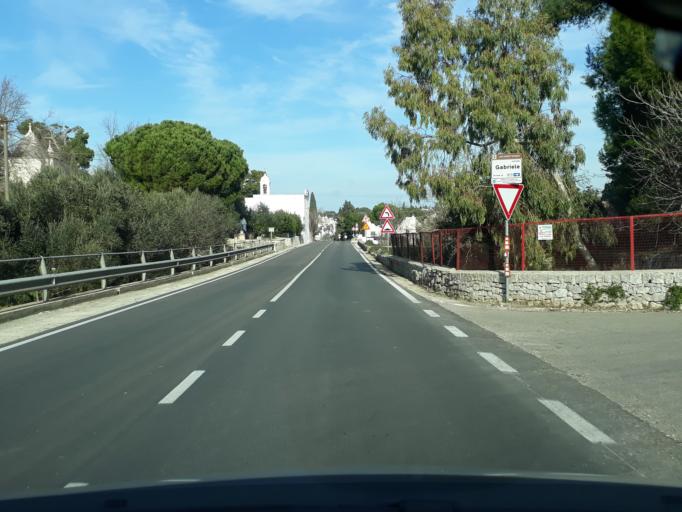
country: IT
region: Apulia
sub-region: Provincia di Brindisi
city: Lamie di Olimpie-Selva
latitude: 40.7924
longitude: 17.3471
